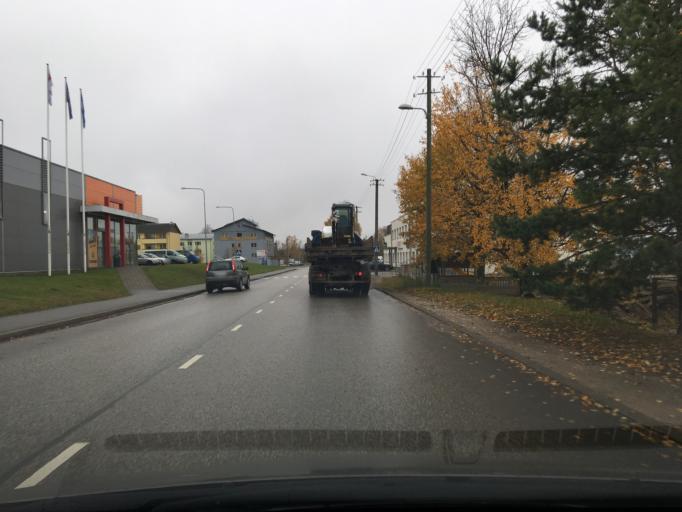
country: EE
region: Tartu
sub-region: Elva linn
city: Elva
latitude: 58.2342
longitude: 26.4154
